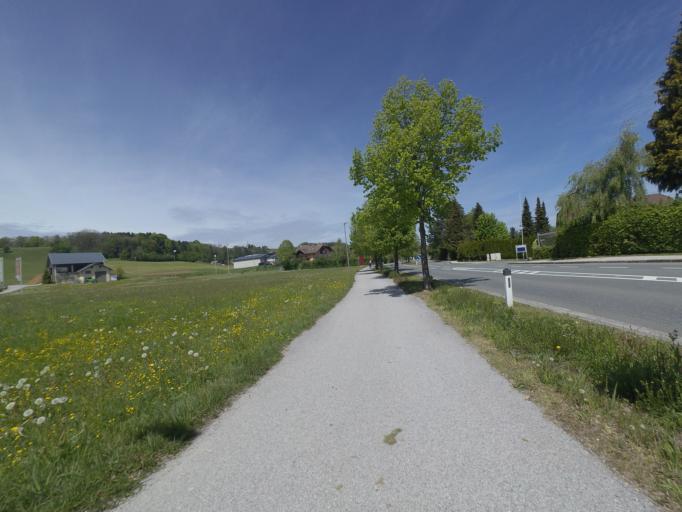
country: AT
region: Salzburg
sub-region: Politischer Bezirk Salzburg-Umgebung
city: Seeham
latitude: 47.9706
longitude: 13.0784
